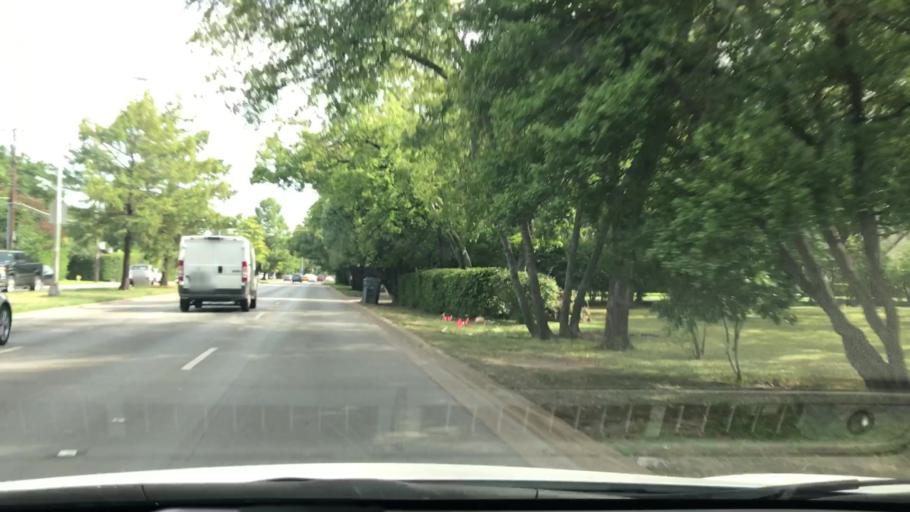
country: US
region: Texas
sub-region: Dallas County
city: University Park
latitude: 32.8400
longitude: -96.8217
